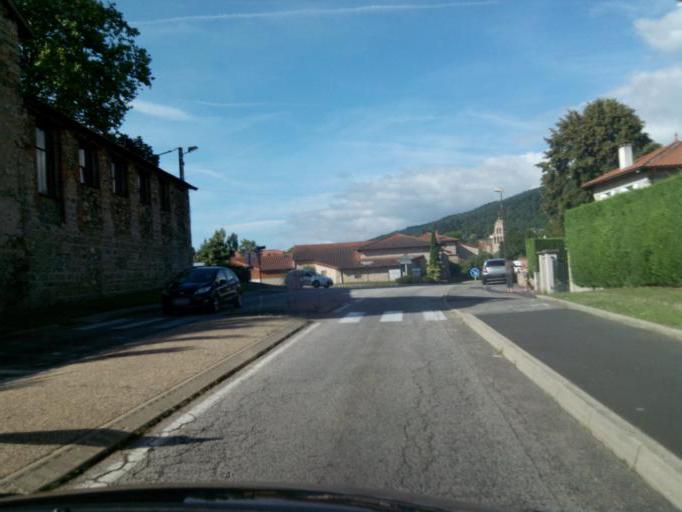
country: FR
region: Auvergne
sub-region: Departement de la Haute-Loire
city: Beauzac
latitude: 45.2611
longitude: 4.1021
